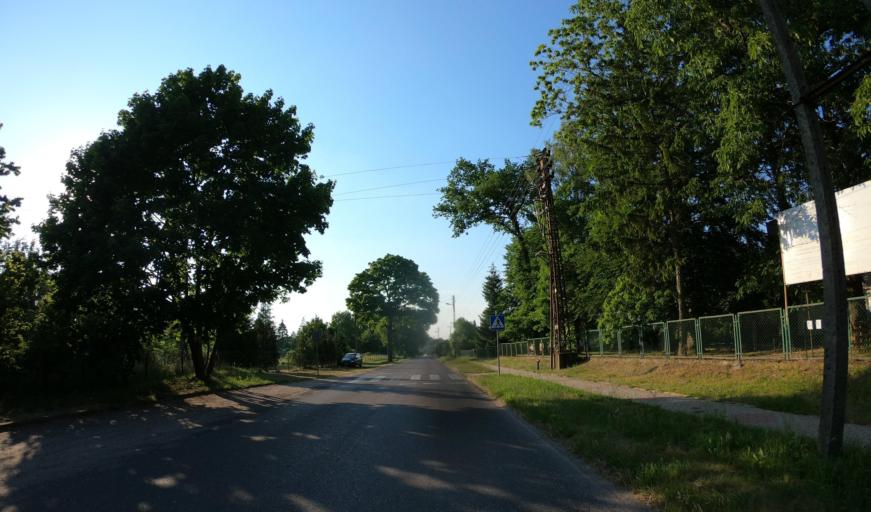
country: PL
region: West Pomeranian Voivodeship
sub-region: Powiat lobeski
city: Resko
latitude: 53.7621
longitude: 15.4079
